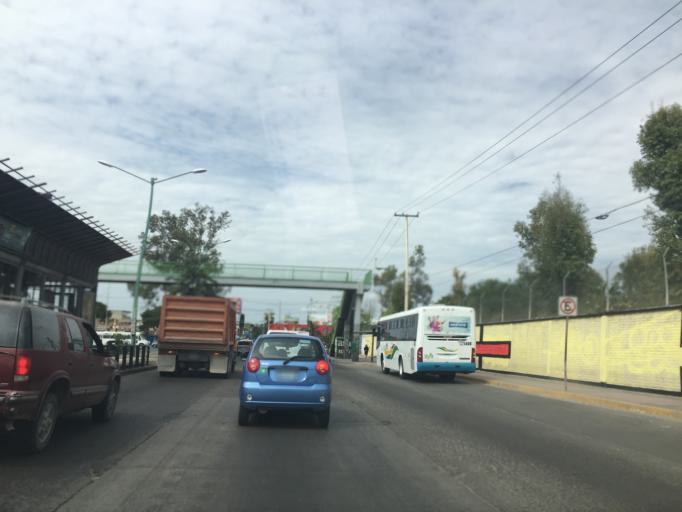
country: MX
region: Guanajuato
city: Leon
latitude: 21.1011
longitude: -101.6780
